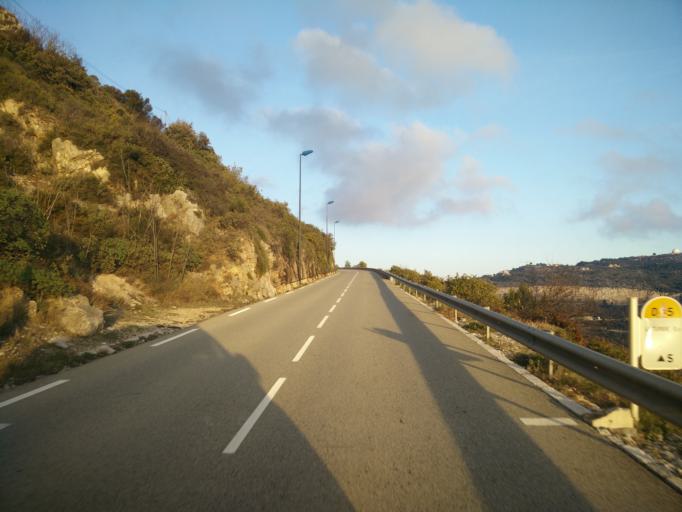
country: FR
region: Provence-Alpes-Cote d'Azur
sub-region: Departement des Alpes-Maritimes
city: La Turbie
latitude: 43.7356
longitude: 7.3821
